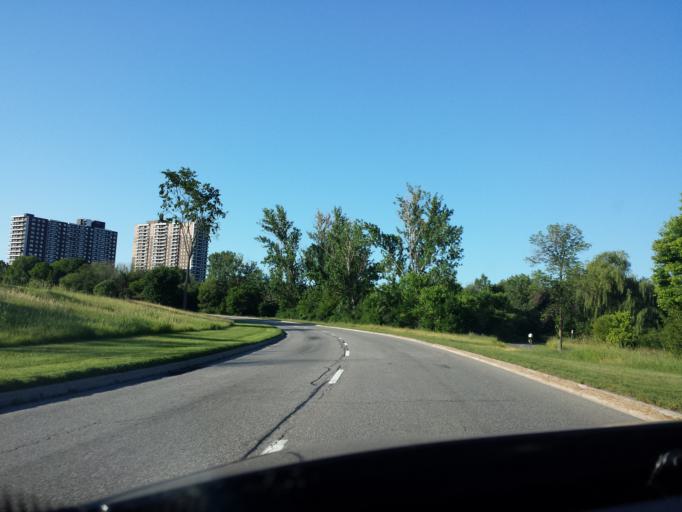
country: CA
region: Ontario
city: Bells Corners
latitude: 45.3734
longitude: -75.7856
